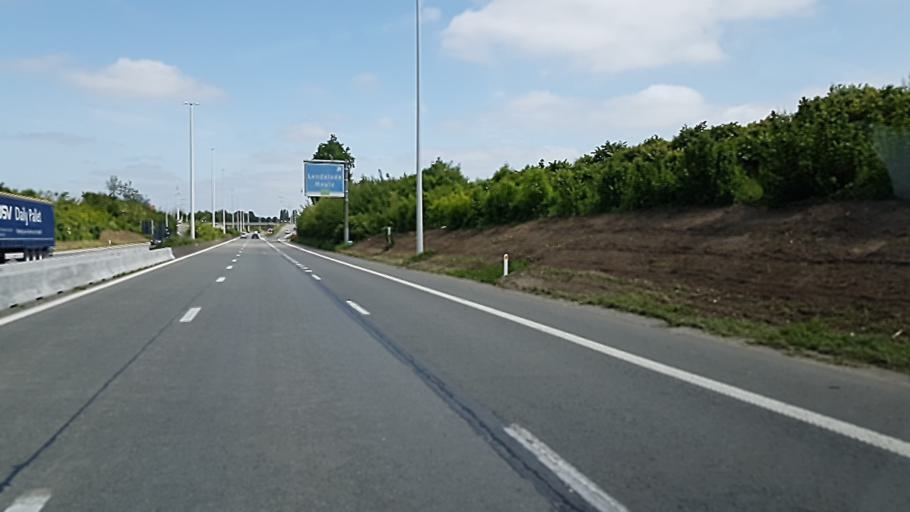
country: BE
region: Flanders
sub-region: Provincie West-Vlaanderen
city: Kortrijk
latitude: 50.8396
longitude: 3.2234
